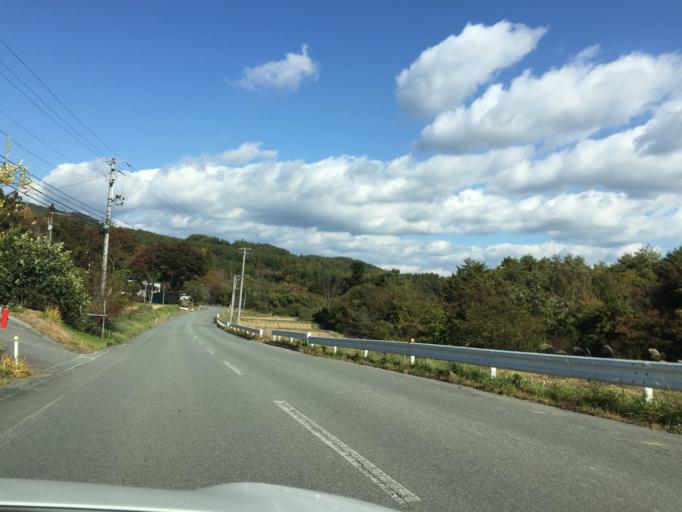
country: JP
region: Fukushima
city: Funehikimachi-funehiki
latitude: 37.3023
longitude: 140.7617
